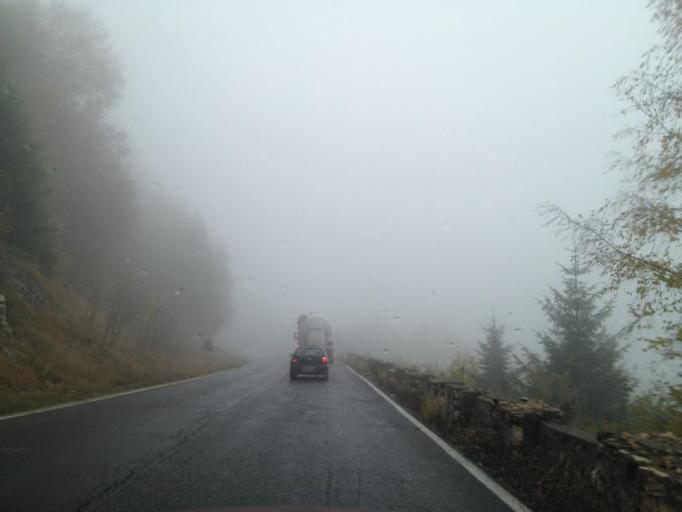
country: RO
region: Arges
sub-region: Comuna Dambovicioara
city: Dambovicioara
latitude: 45.4257
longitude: 25.2538
